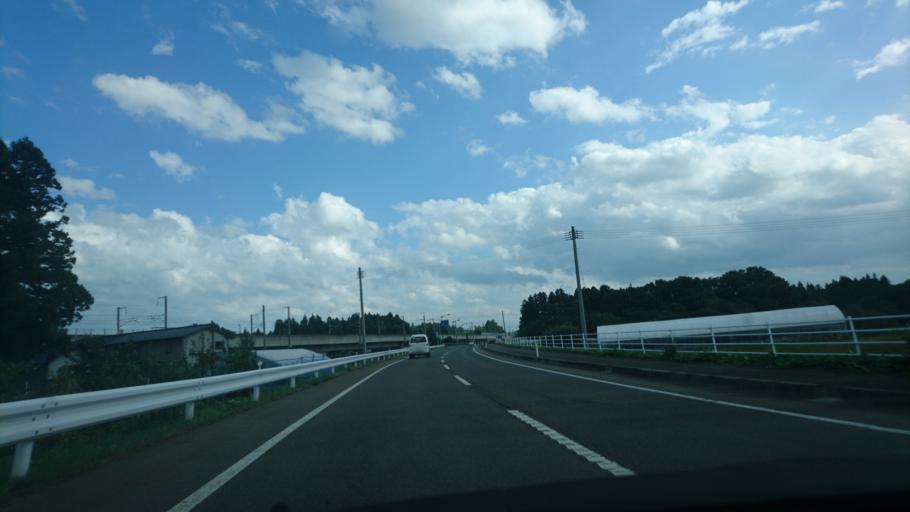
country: JP
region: Iwate
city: Hanamaki
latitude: 39.4571
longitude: 141.1746
